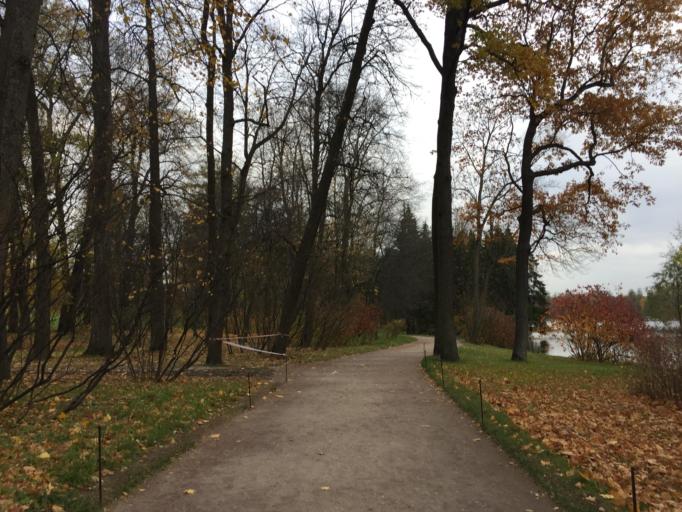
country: RU
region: St.-Petersburg
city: Pushkin
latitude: 59.7106
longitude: 30.3892
